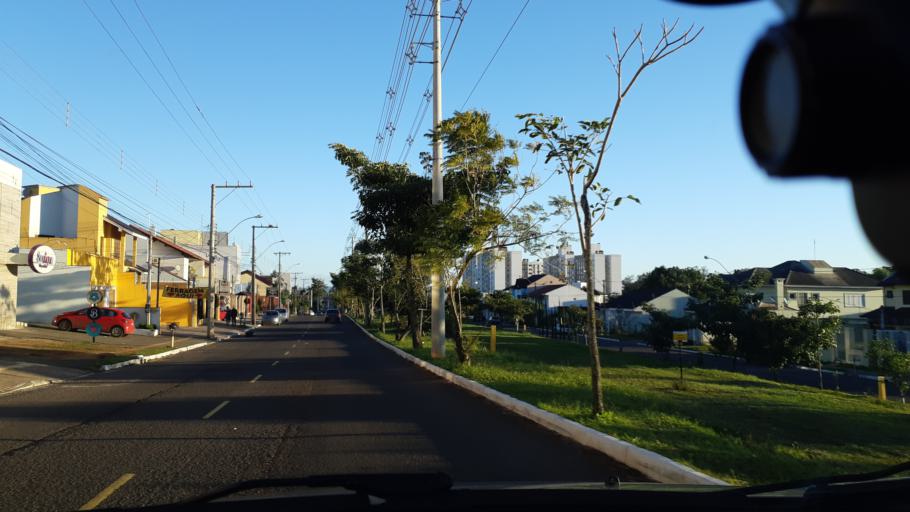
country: BR
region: Rio Grande do Sul
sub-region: Canoas
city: Canoas
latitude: -29.9153
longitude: -51.1543
